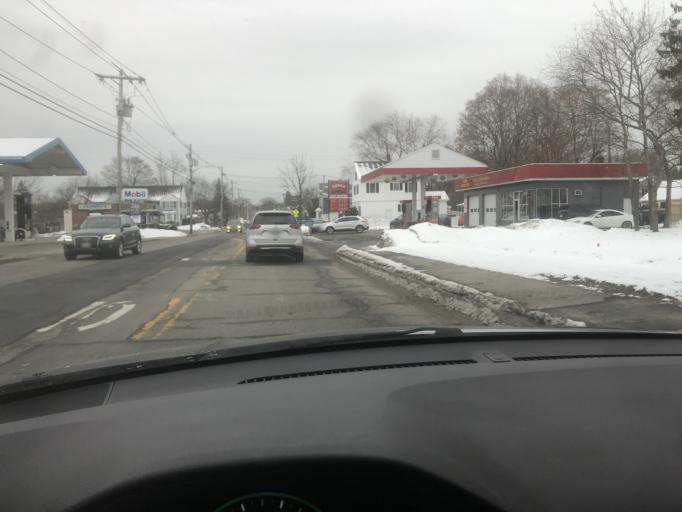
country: US
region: Massachusetts
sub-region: Middlesex County
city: Tewksbury
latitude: 42.6116
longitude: -71.2327
